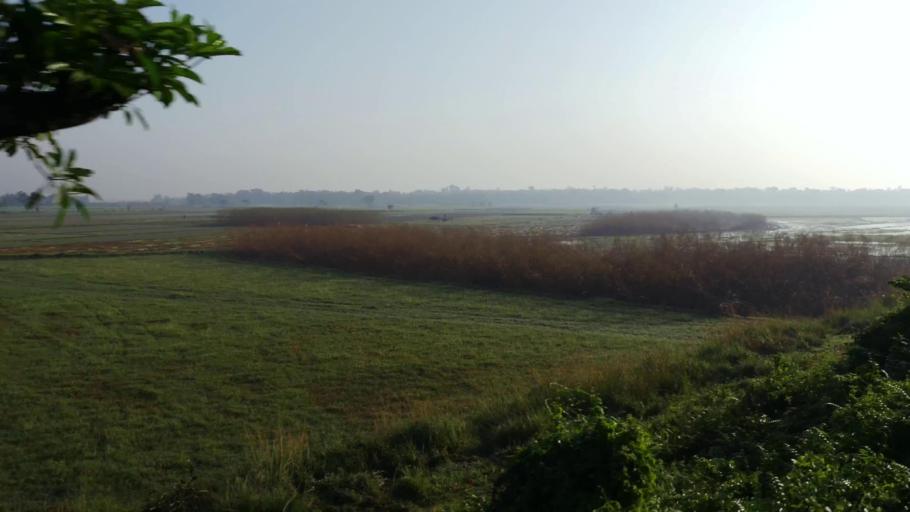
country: BD
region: Dhaka
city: Jamalpur
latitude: 24.9205
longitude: 89.9420
